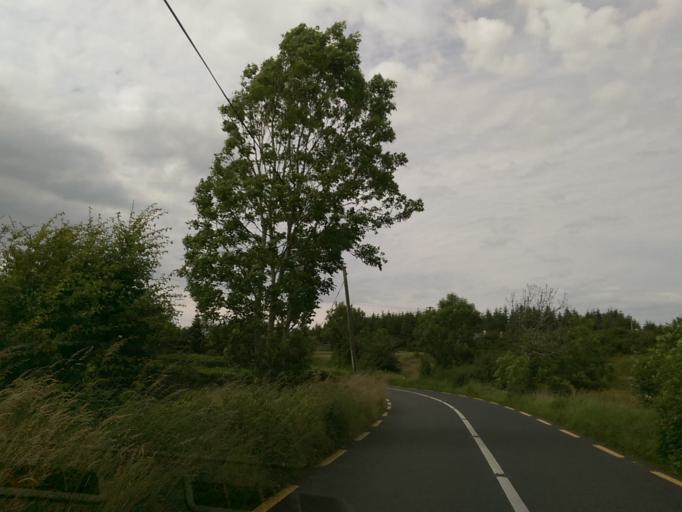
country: IE
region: Connaught
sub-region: County Galway
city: Bearna
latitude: 52.9938
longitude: -9.3039
